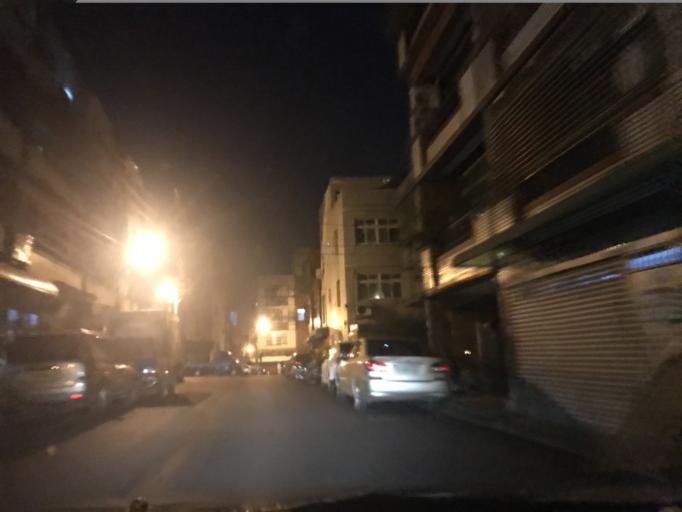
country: TW
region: Taiwan
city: Taoyuan City
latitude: 24.9523
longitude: 121.2105
